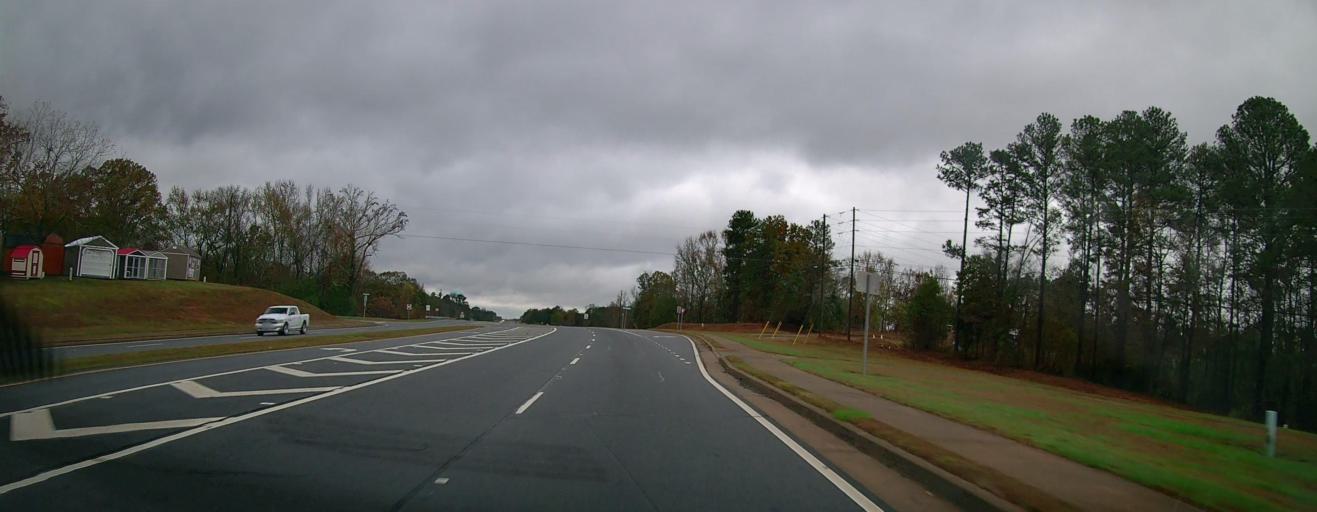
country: US
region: Georgia
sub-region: Jackson County
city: Nicholson
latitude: 34.1321
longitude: -83.4283
